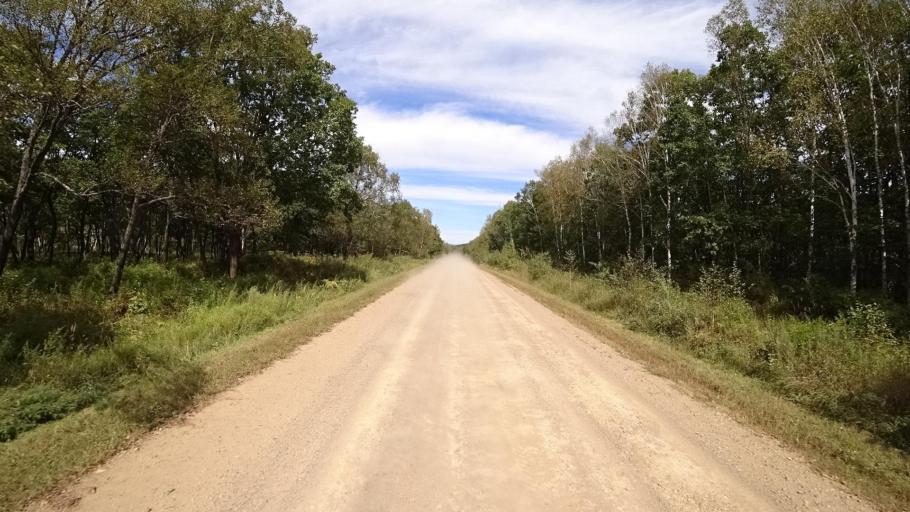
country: RU
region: Primorskiy
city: Yakovlevka
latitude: 44.6896
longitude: 133.6185
